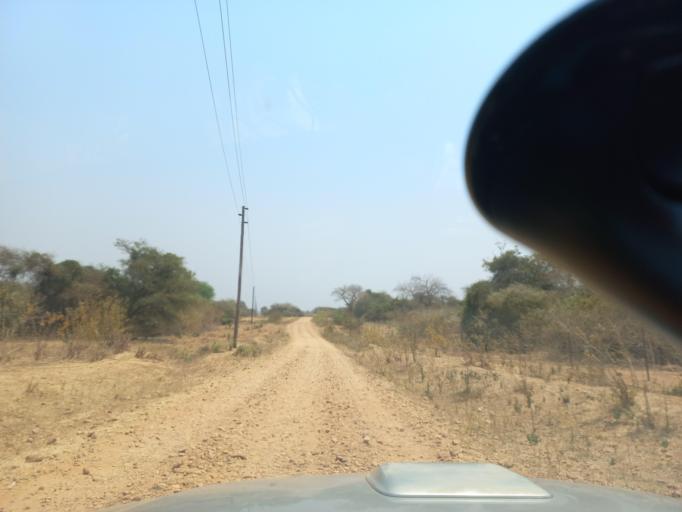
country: ZW
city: Chirundu
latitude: -15.9321
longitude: 28.8677
